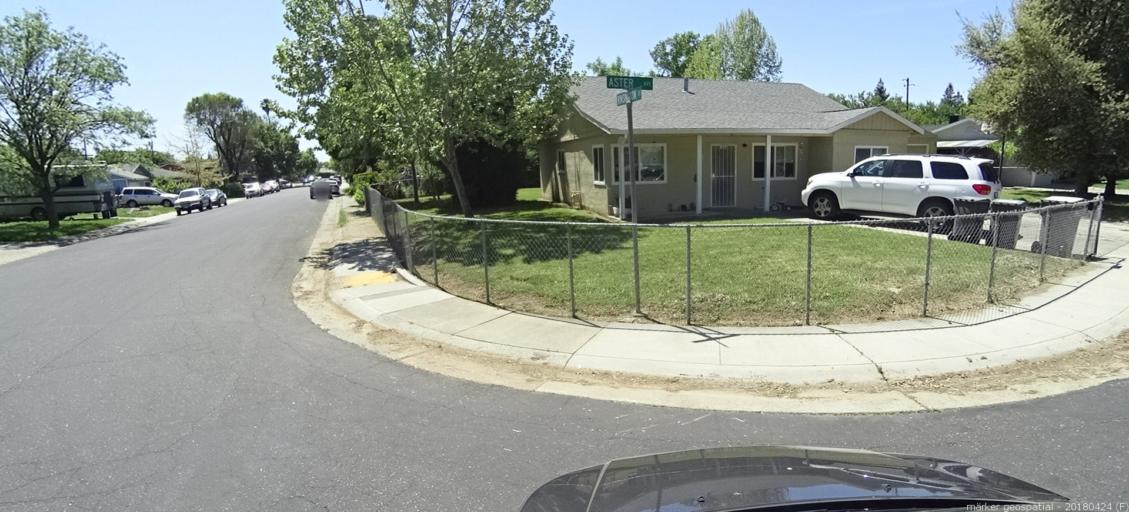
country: US
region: California
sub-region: Yolo County
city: West Sacramento
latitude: 38.5590
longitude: -121.5340
